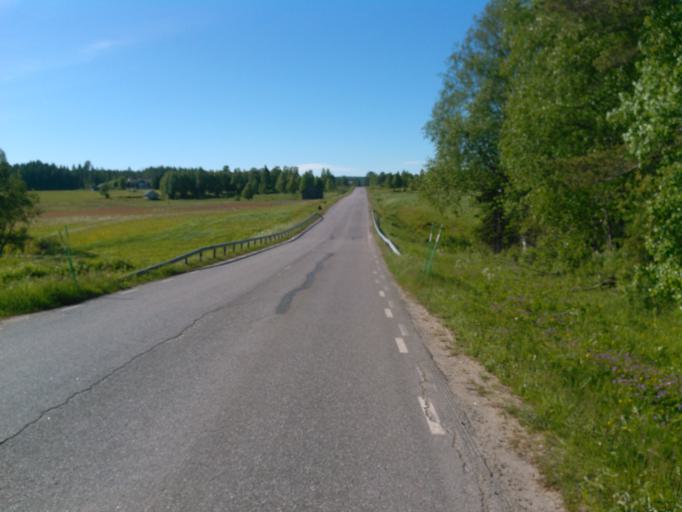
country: SE
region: Vaesterbotten
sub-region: Umea Kommun
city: Roback
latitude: 63.8236
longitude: 20.1262
